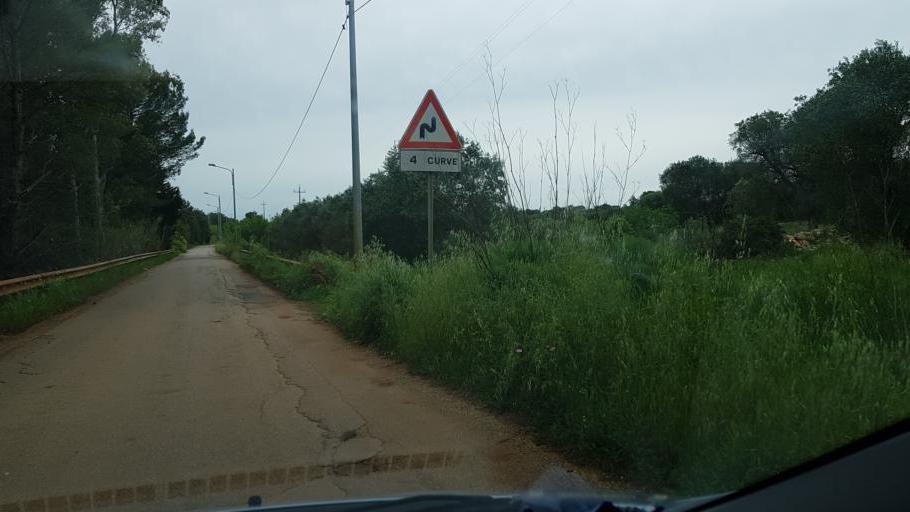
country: IT
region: Apulia
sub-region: Provincia di Brindisi
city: San Vito dei Normanni
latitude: 40.6640
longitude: 17.7335
